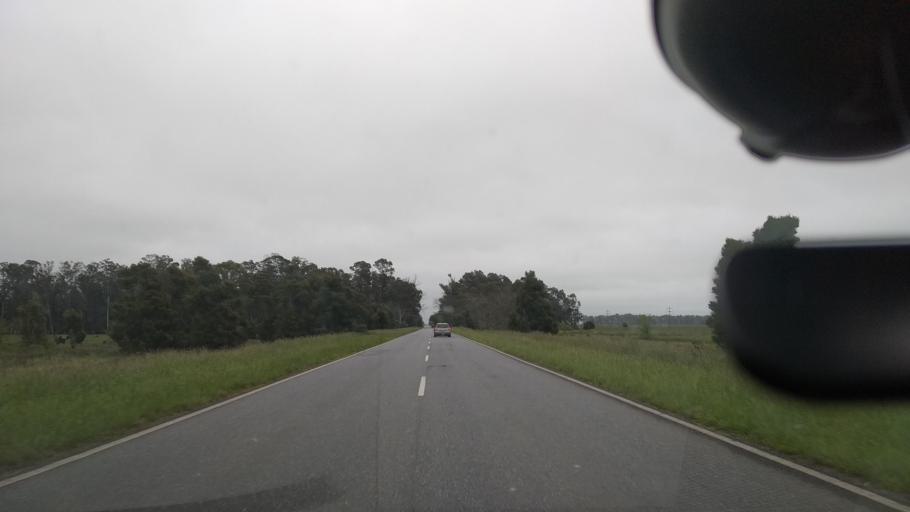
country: AR
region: Buenos Aires
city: Veronica
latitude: -35.3192
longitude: -57.4790
